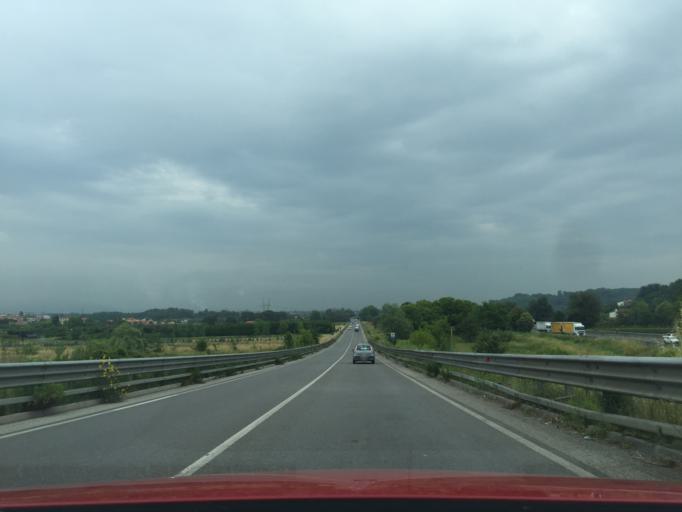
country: IT
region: Tuscany
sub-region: Provincia di Pistoia
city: Stazione Masotti
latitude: 43.9122
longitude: 10.8655
